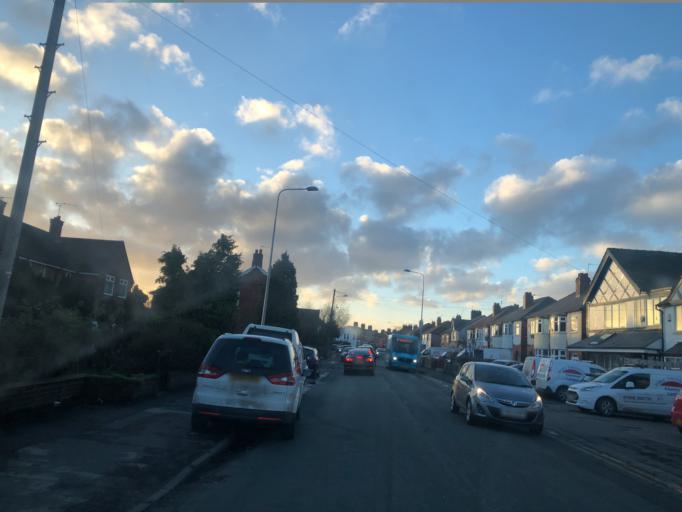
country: GB
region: England
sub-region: Cheshire West and Chester
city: Marston
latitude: 53.2571
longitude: -2.4852
